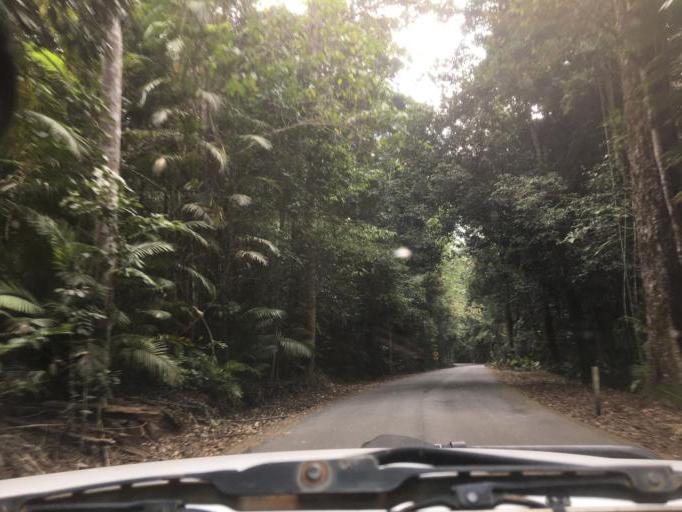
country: AU
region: Queensland
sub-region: Tablelands
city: Tolga
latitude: -17.2793
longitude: 145.6260
